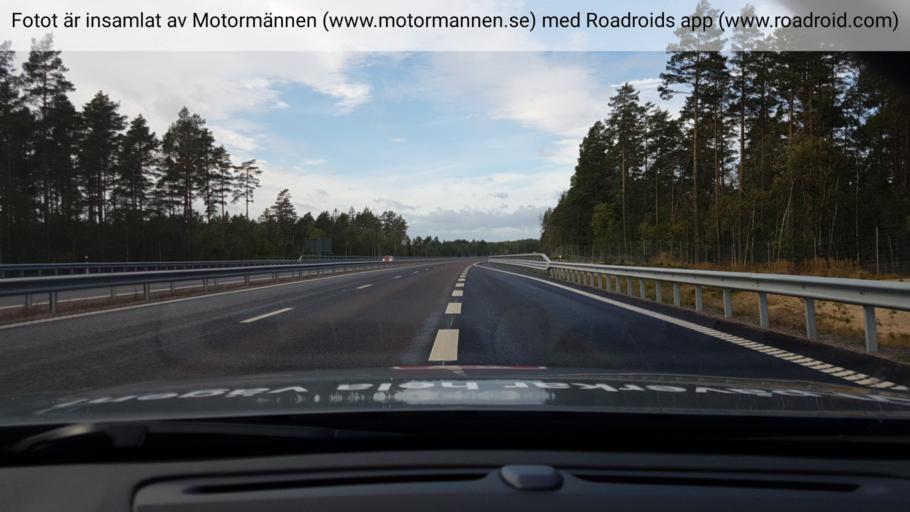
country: SE
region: Vaermland
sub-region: Kils Kommun
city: Kil
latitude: 59.3845
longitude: 13.3273
